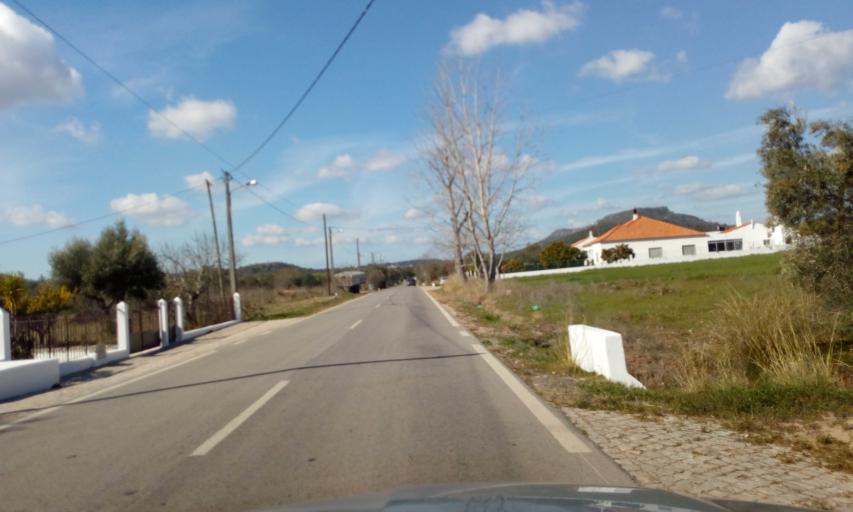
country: PT
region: Faro
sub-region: Loule
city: Loule
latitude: 37.2442
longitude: -8.0524
